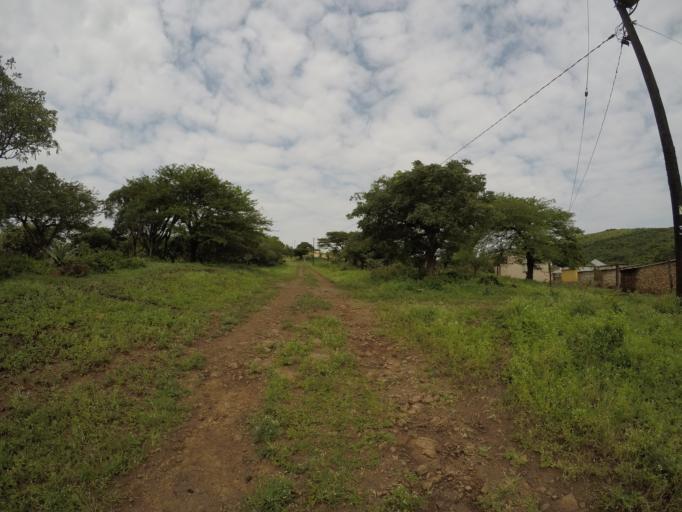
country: ZA
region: KwaZulu-Natal
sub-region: uThungulu District Municipality
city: Empangeni
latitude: -28.6262
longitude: 31.9106
